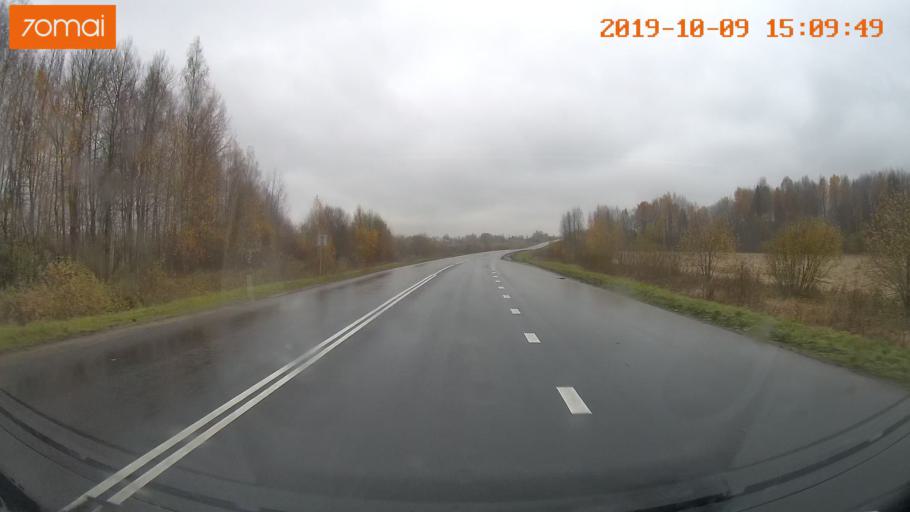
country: RU
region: Kostroma
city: Susanino
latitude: 58.1861
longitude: 41.6483
